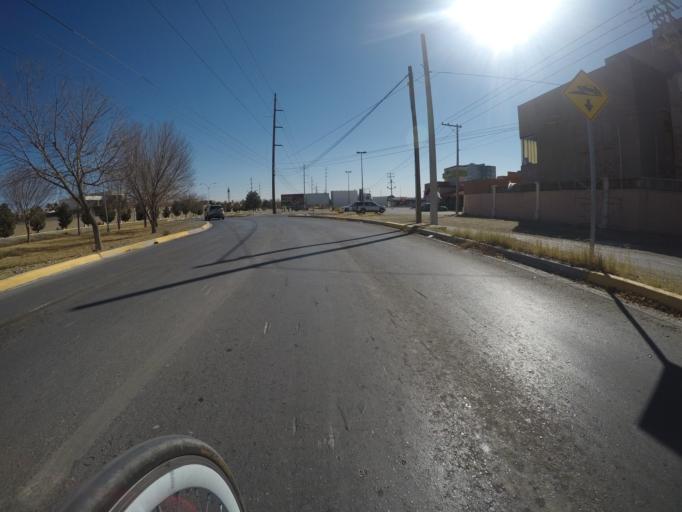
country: MX
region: Chihuahua
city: Ciudad Juarez
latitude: 31.7076
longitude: -106.3897
